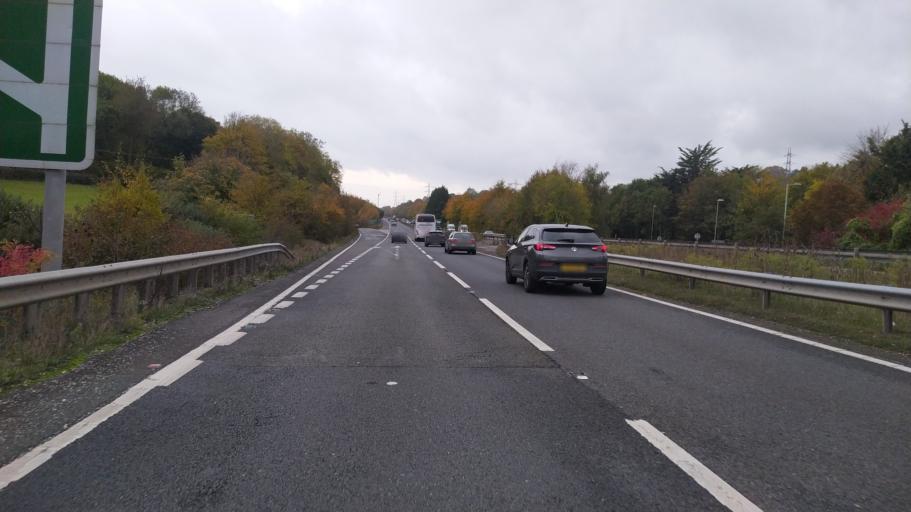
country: GB
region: England
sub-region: Hampshire
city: Cowplain
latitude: 50.9239
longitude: -0.9976
